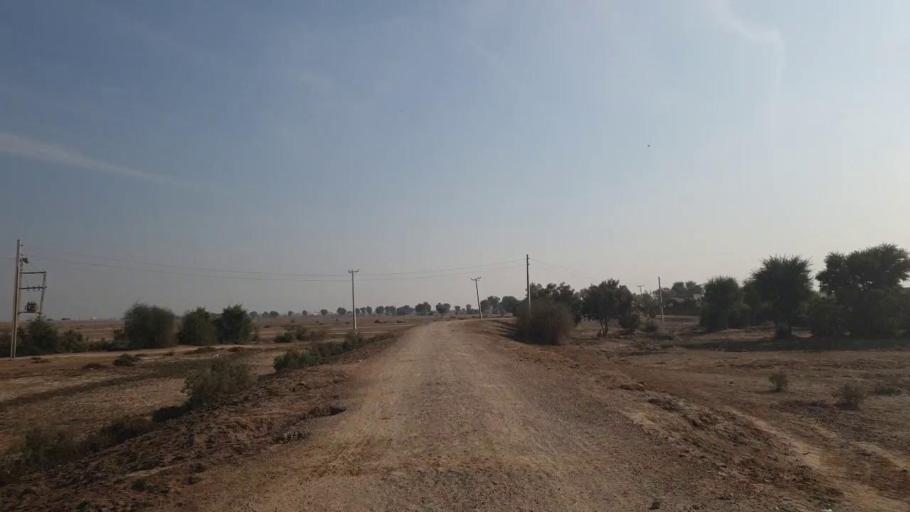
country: PK
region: Sindh
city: Sann
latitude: 25.9250
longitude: 68.2193
